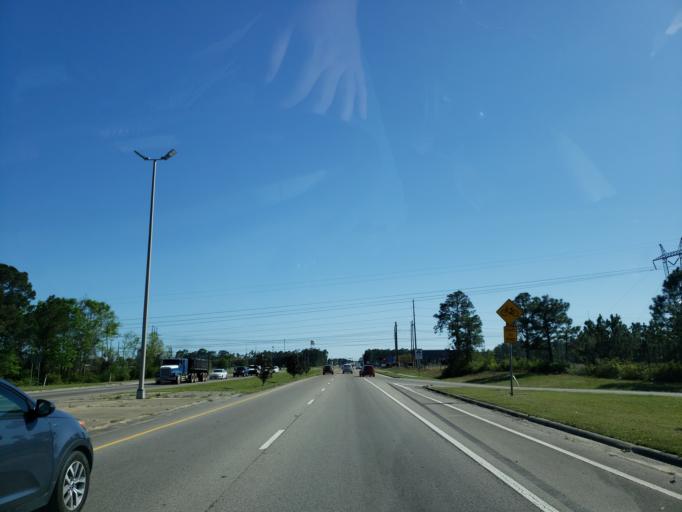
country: US
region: Mississippi
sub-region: Harrison County
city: West Gulfport
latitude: 30.4434
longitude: -89.0313
